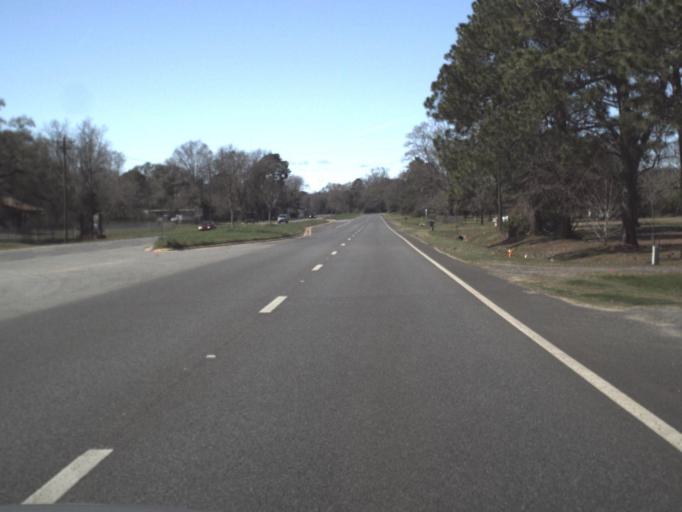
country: US
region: Florida
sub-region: Gadsden County
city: Quincy
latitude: 30.5876
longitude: -84.6209
